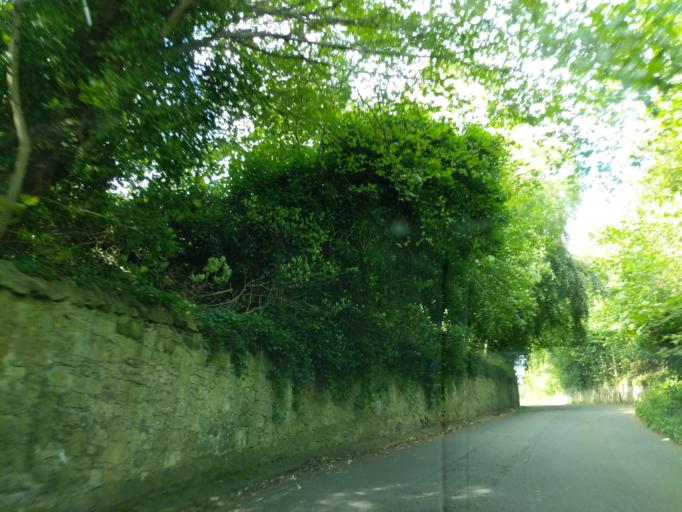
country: GB
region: Scotland
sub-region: Midlothian
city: Loanhead
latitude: 55.8737
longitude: -3.1448
